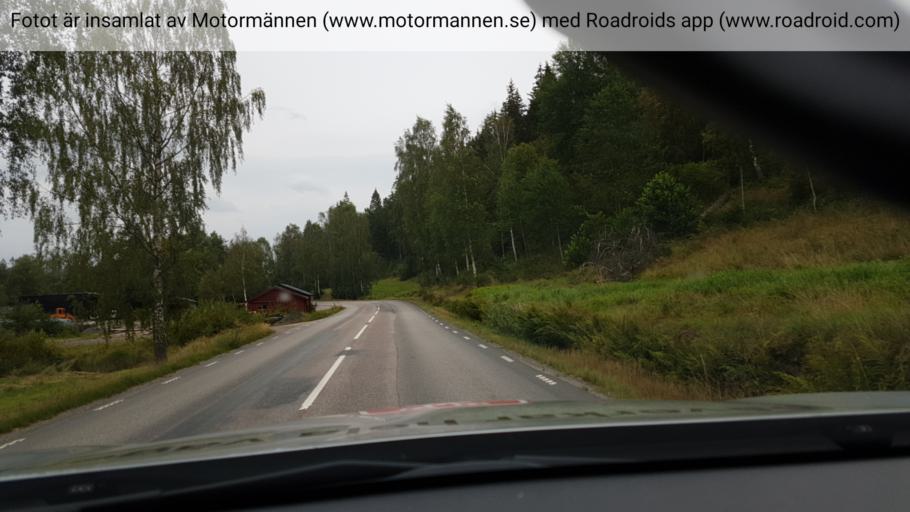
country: SE
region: Vaestra Goetaland
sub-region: Harryda Kommun
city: Hindas
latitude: 57.6086
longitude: 12.3466
